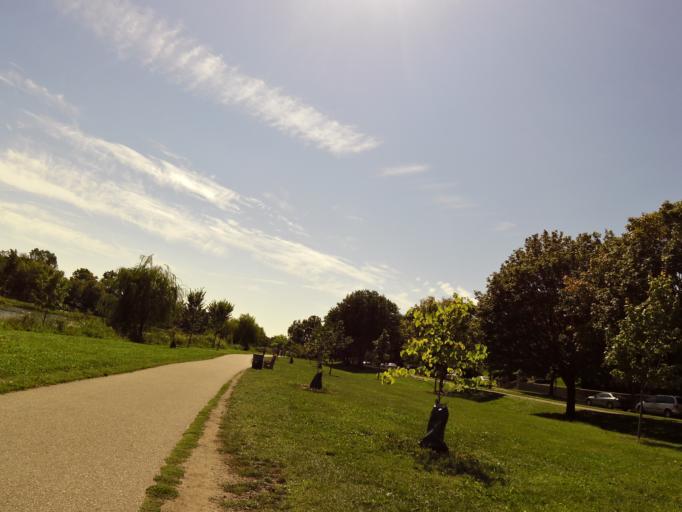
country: US
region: Minnesota
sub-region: Hennepin County
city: Minneapolis
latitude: 44.9605
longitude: -93.3040
